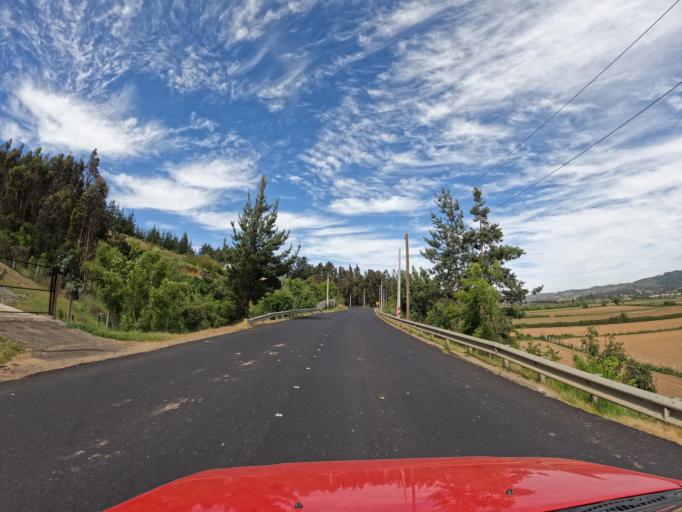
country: CL
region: Maule
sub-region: Provincia de Talca
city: Constitucion
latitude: -35.0786
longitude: -72.0326
